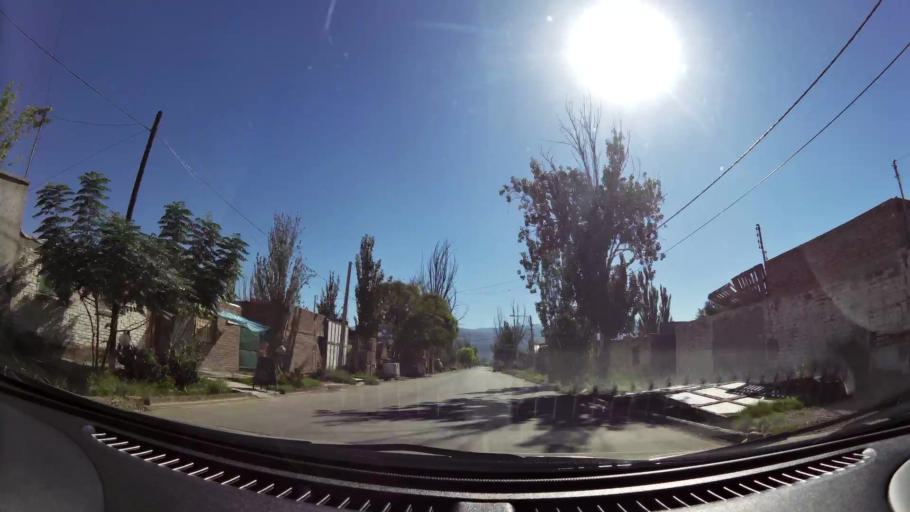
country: AR
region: Mendoza
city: Las Heras
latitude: -32.8365
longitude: -68.8072
